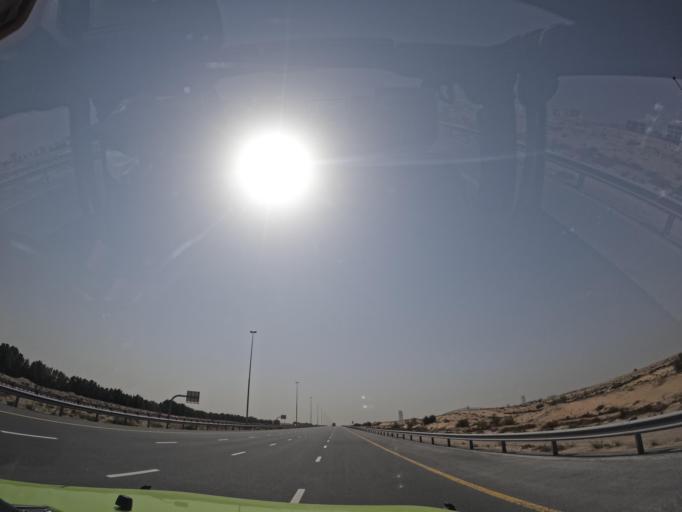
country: AE
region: Dubai
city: Dubai
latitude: 25.0938
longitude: 55.3601
